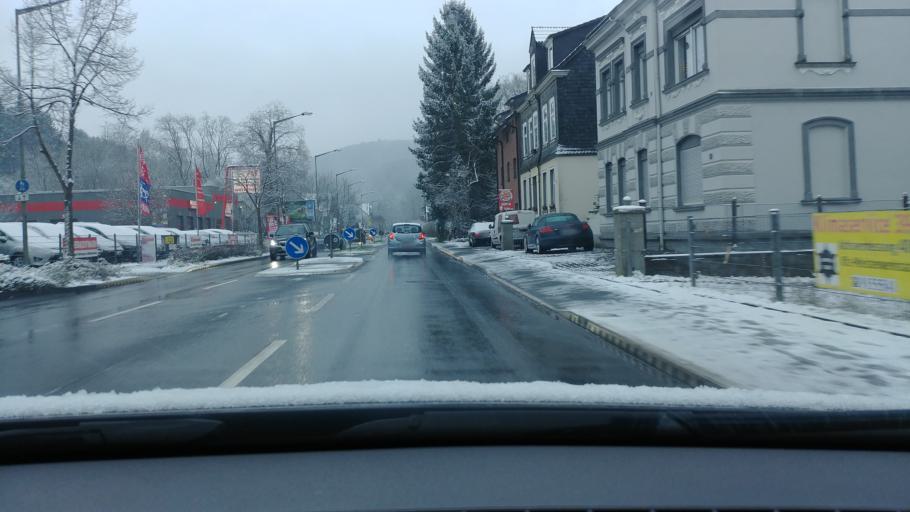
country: DE
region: North Rhine-Westphalia
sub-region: Regierungsbezirk Koln
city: Gummersbach
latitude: 50.9905
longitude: 7.5578
